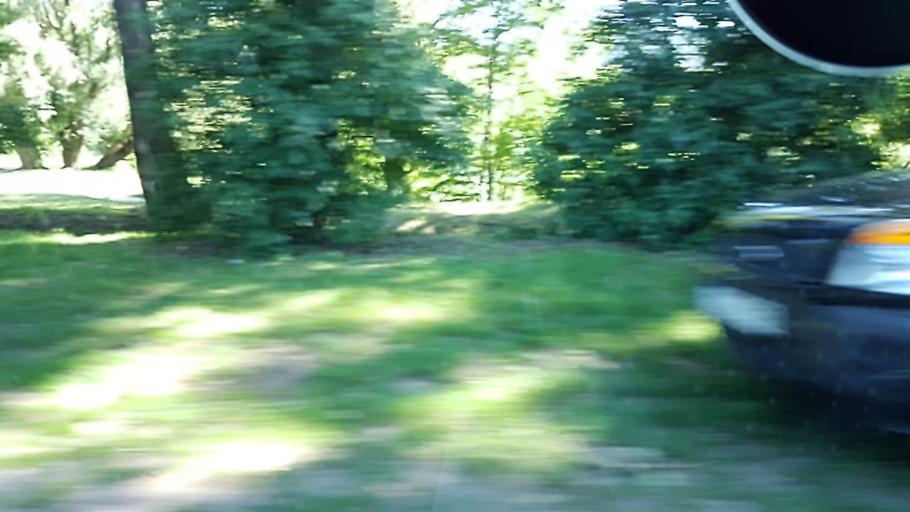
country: HU
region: Pest
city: Pilisvorosvar
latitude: 47.6079
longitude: 18.9099
